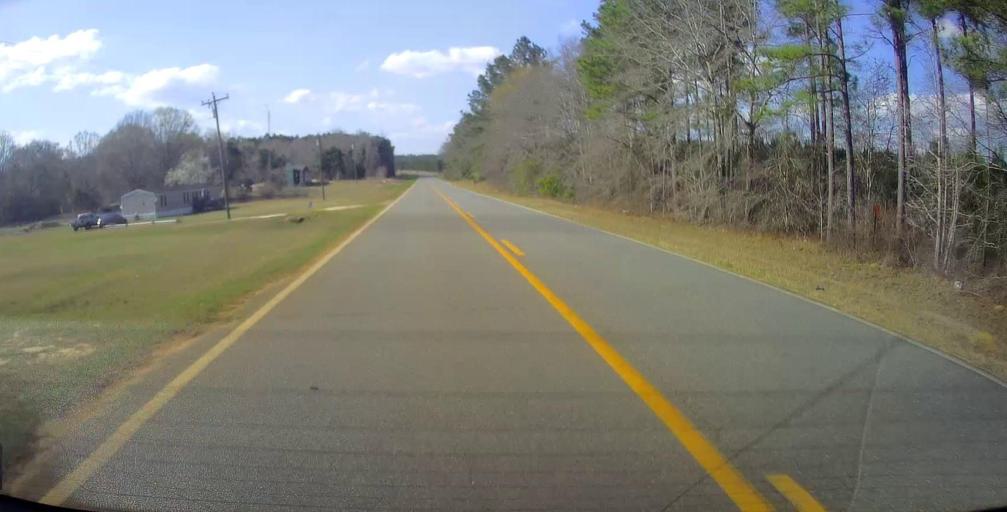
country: US
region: Georgia
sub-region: Laurens County
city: Dublin
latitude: 32.5810
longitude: -83.0526
